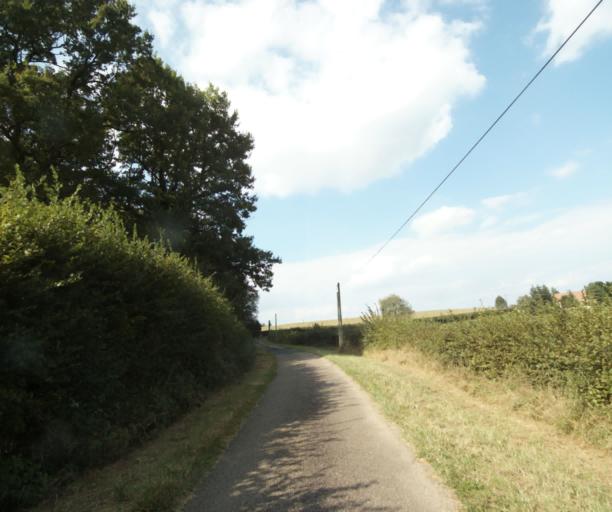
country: FR
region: Bourgogne
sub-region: Departement de Saone-et-Loire
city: Palinges
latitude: 46.4885
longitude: 4.2253
